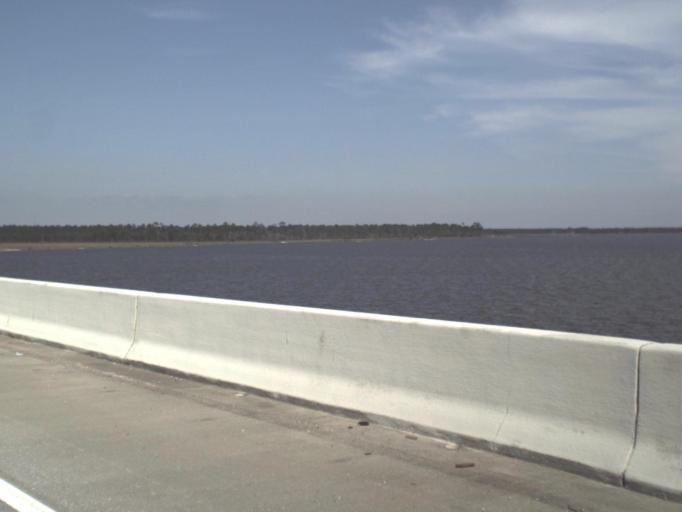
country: US
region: Florida
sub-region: Santa Rosa County
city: Pace
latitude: 30.5272
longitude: -87.1324
